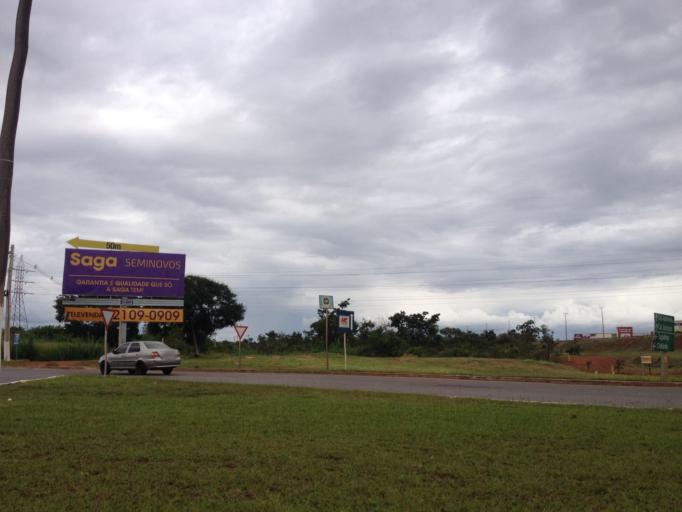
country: BR
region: Federal District
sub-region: Brasilia
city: Brasilia
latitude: -15.7947
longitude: -47.9700
